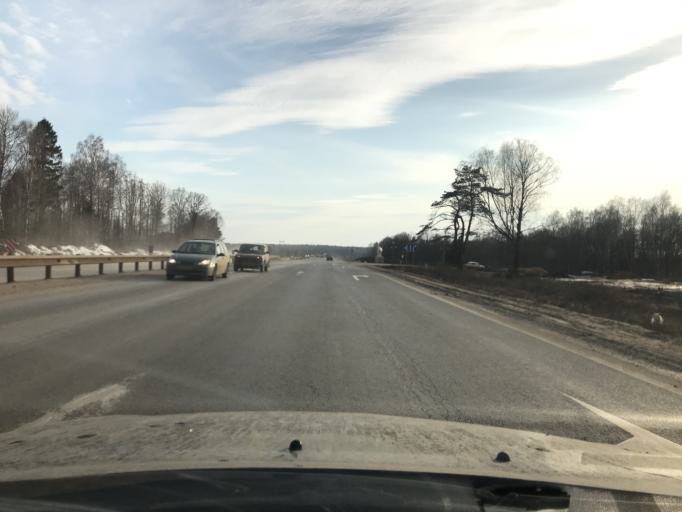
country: RU
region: Kaluga
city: Kaluga
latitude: 54.4329
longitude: 36.2143
